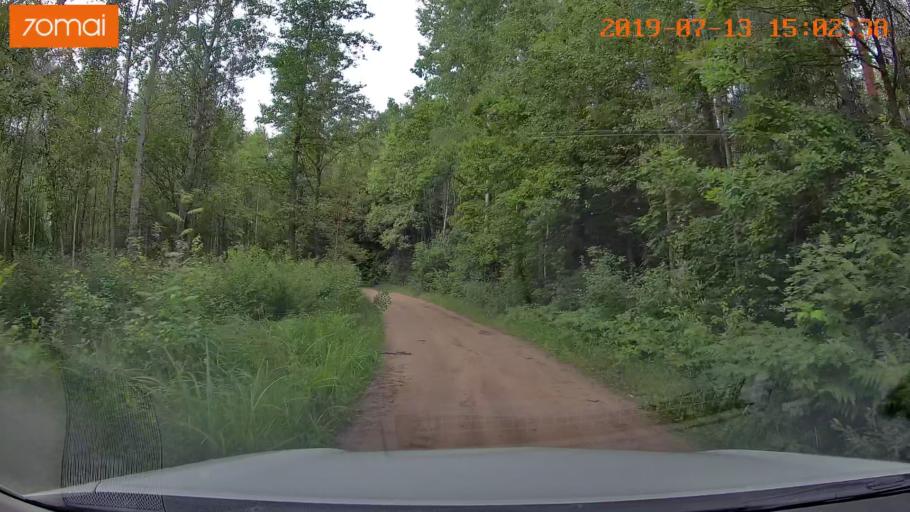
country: BY
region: Mogilev
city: Asipovichy
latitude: 53.2119
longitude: 28.7514
